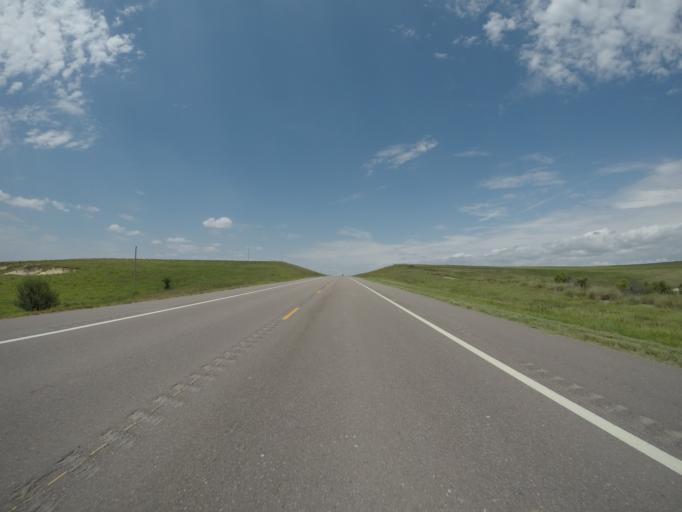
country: US
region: Kansas
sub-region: Graham County
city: Hill City
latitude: 39.3795
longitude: -99.7006
